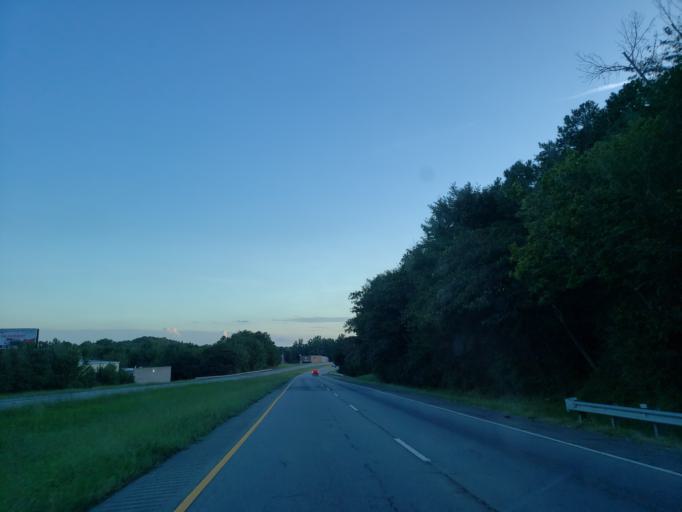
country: US
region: Georgia
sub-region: Floyd County
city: Lindale
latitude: 34.2034
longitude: -85.1939
